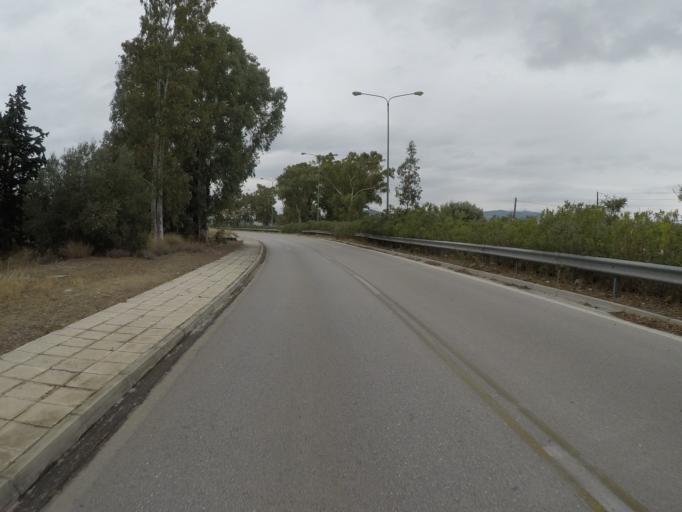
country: GR
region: Peloponnese
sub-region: Nomos Korinthias
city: Korinthos
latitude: 37.9413
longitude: 22.9791
